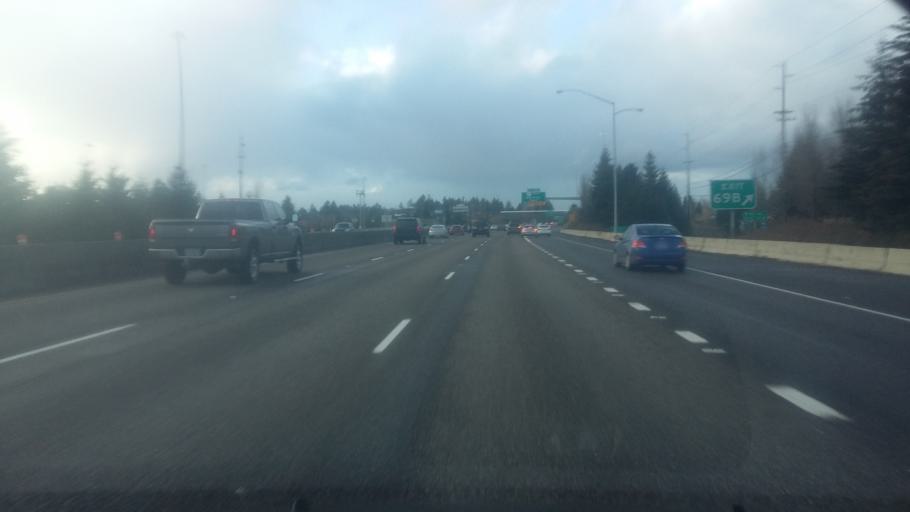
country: US
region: Oregon
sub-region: Washington County
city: West Haven-Sylvan
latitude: 45.5075
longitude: -122.7750
